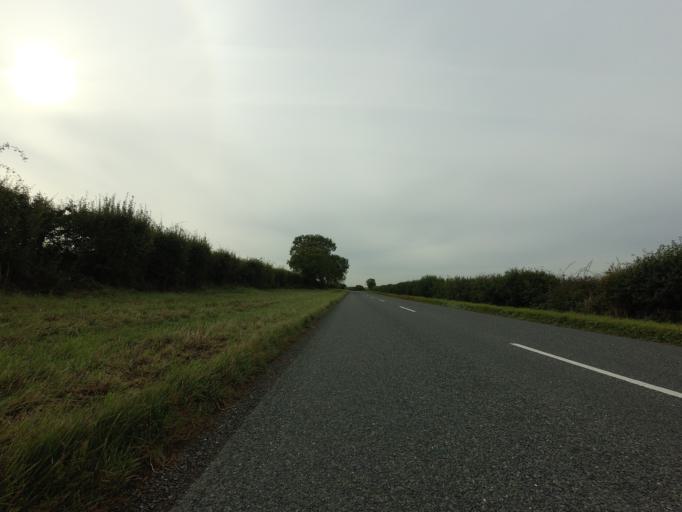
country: GB
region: England
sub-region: Cambridgeshire
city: Melbourn
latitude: 52.0487
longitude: 0.0460
